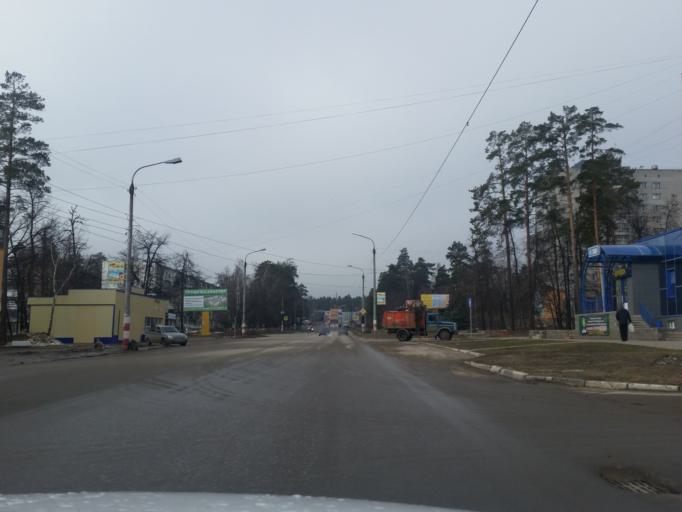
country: RU
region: Ulyanovsk
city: Dimitrovgrad
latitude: 54.2365
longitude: 49.5619
